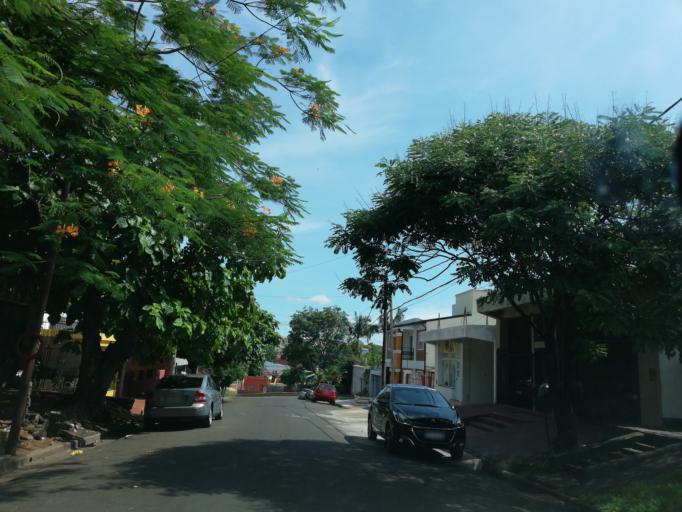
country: AR
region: Misiones
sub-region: Departamento de Capital
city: Posadas
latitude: -27.3778
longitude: -55.8895
